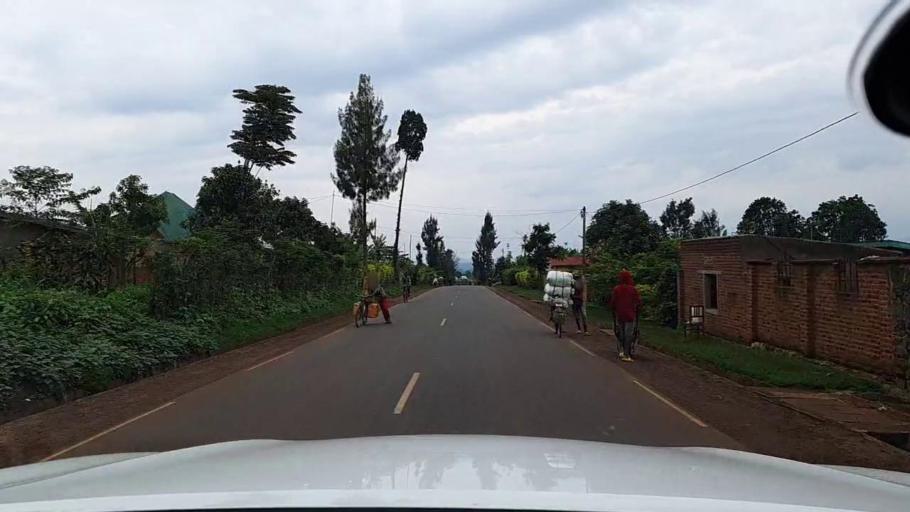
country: RW
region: Western Province
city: Cyangugu
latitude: -2.5993
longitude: 28.9327
